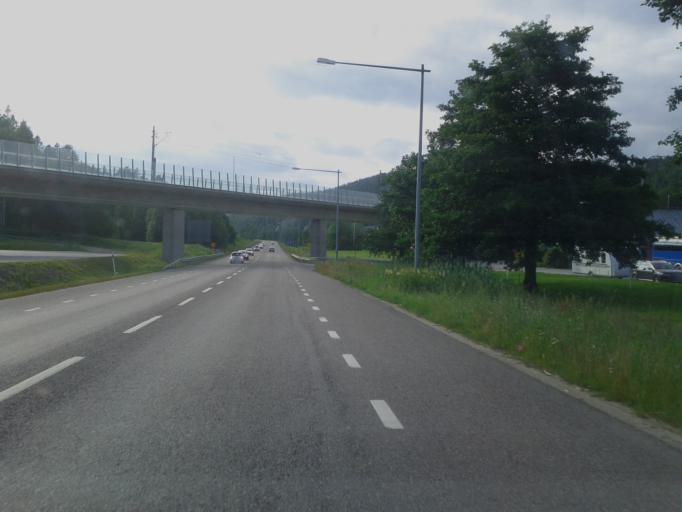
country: SE
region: Vaesternorrland
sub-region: OErnskoeldsviks Kommun
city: Ornskoldsvik
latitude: 63.2917
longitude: 18.7040
